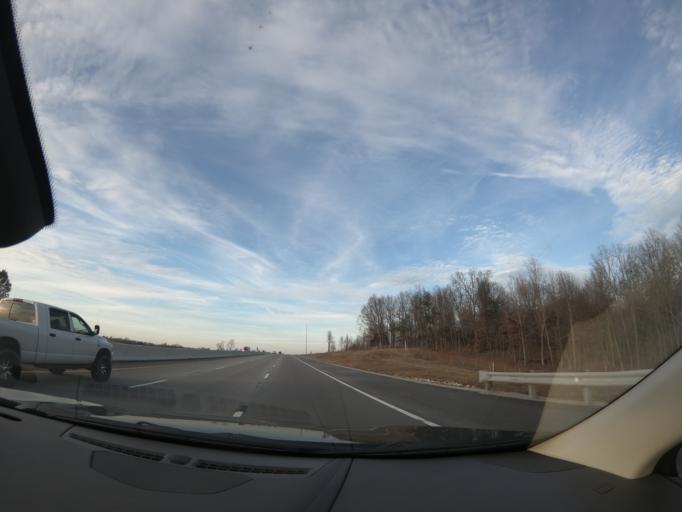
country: US
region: Kentucky
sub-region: Larue County
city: Hodgenville
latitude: 37.4792
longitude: -85.8811
